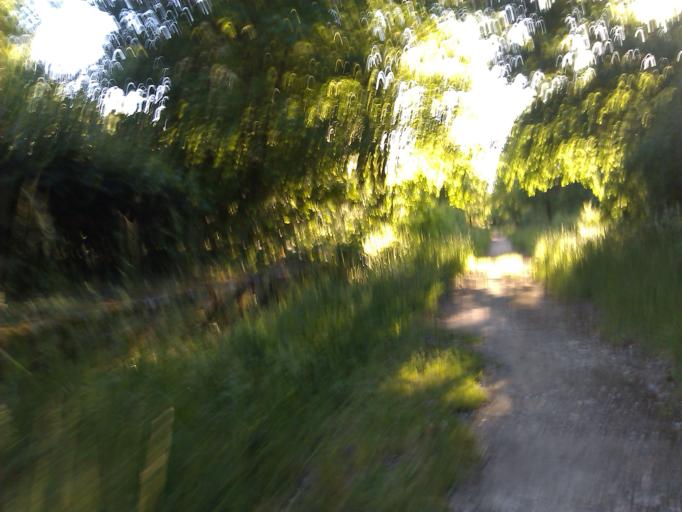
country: FR
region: Centre
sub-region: Departement de l'Indre
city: Le Blanc
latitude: 46.6006
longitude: 1.0134
